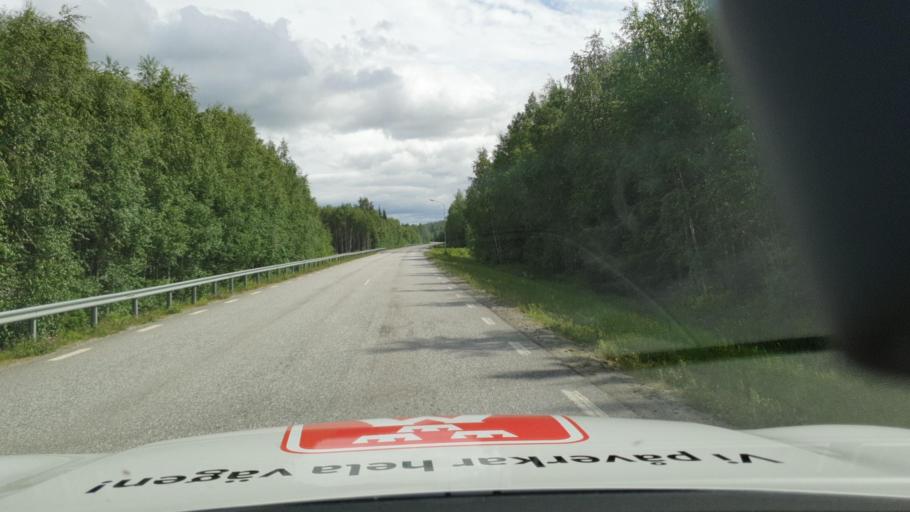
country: SE
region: Vaesterbotten
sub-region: Dorotea Kommun
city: Dorotea
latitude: 64.2485
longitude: 16.6737
